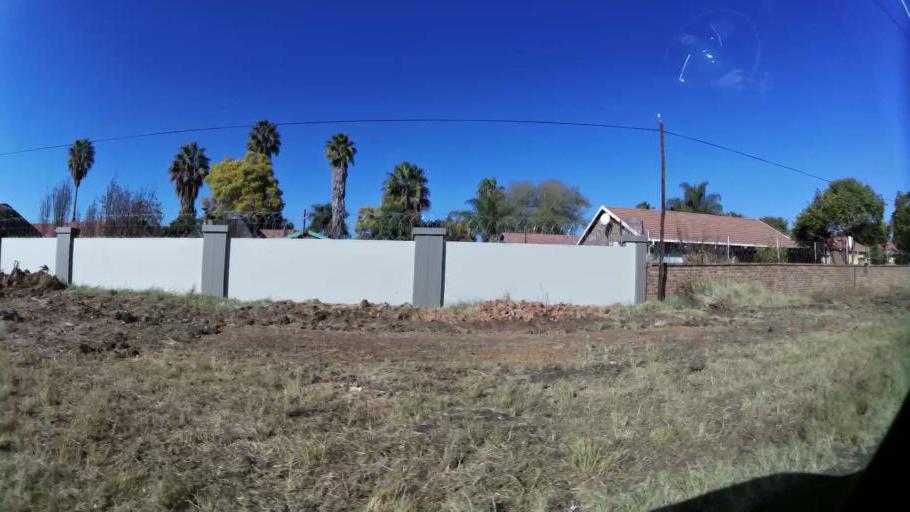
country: ZA
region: Gauteng
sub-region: City of Tshwane Metropolitan Municipality
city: Pretoria
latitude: -25.6669
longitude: 28.1350
